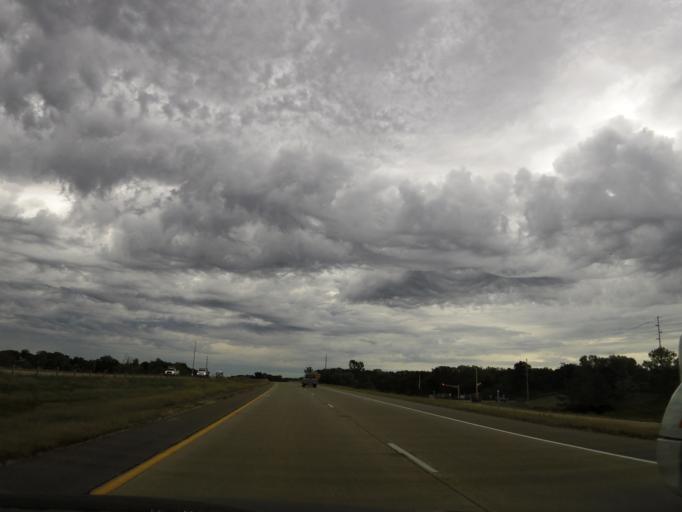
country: US
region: Minnesota
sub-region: Dakota County
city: Burnsville
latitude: 44.7579
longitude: -93.2507
